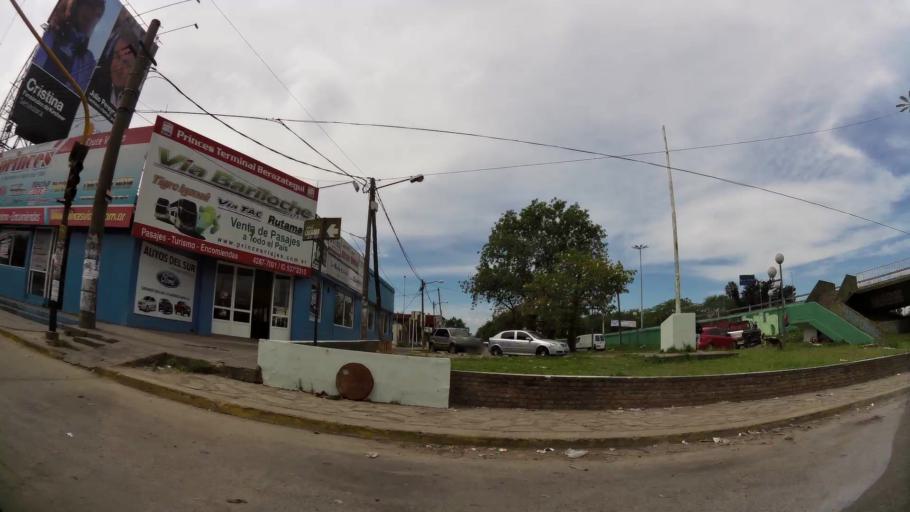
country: AR
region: Buenos Aires
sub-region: Partido de Quilmes
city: Quilmes
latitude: -34.7803
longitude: -58.2620
